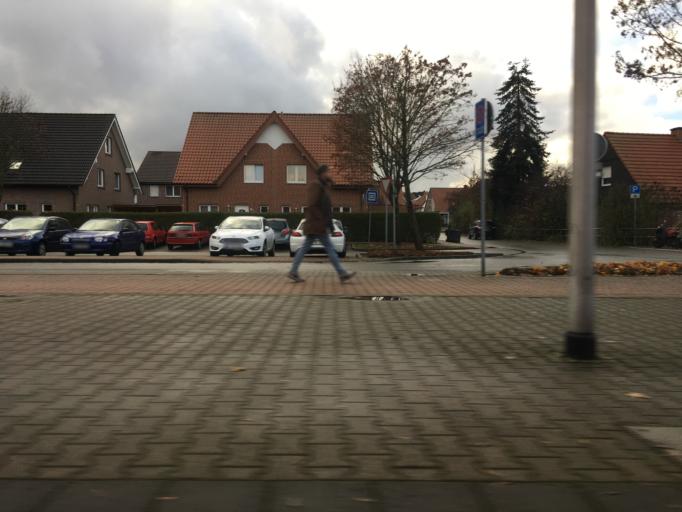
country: DE
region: North Rhine-Westphalia
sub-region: Regierungsbezirk Munster
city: Altenberge
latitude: 52.0518
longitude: 7.4815
